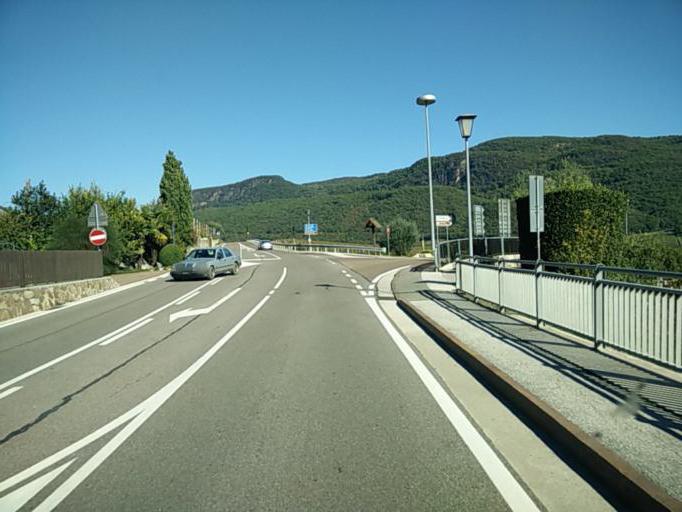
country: IT
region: Trentino-Alto Adige
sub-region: Bolzano
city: Caldaro sulla Strada del Vino
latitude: 46.3861
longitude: 11.2545
